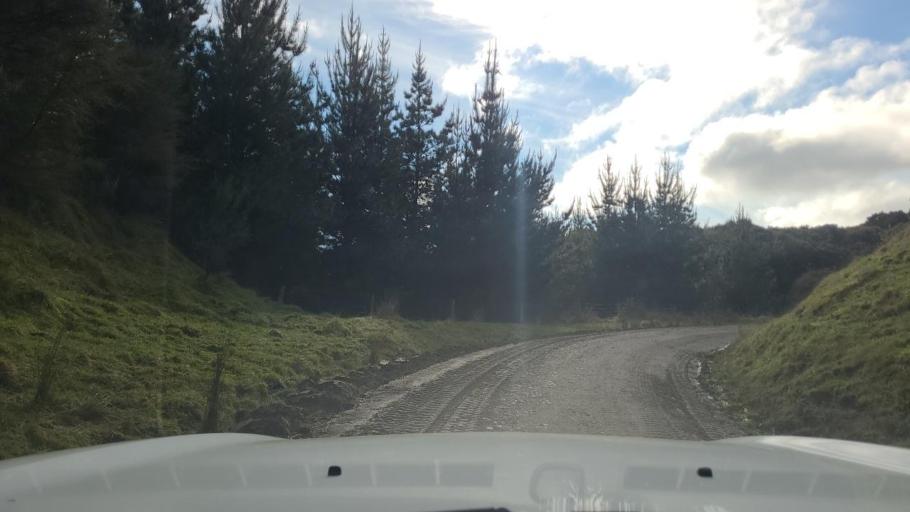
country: NZ
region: Wellington
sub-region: South Wairarapa District
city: Waipawa
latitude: -41.2401
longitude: 175.6998
